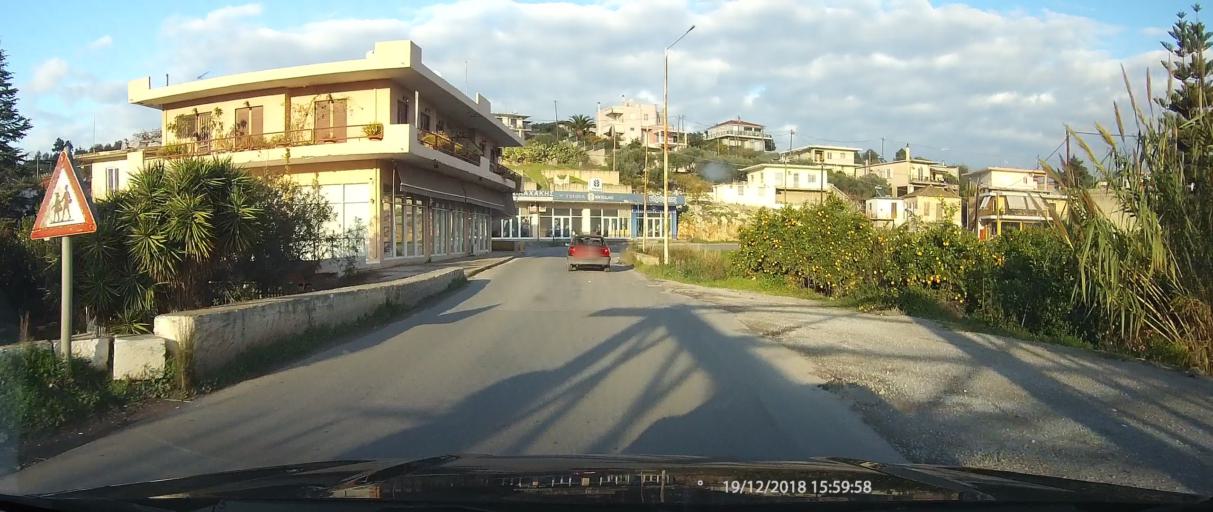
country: GR
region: Peloponnese
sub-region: Nomos Lakonias
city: Skala
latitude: 36.8548
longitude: 22.6753
